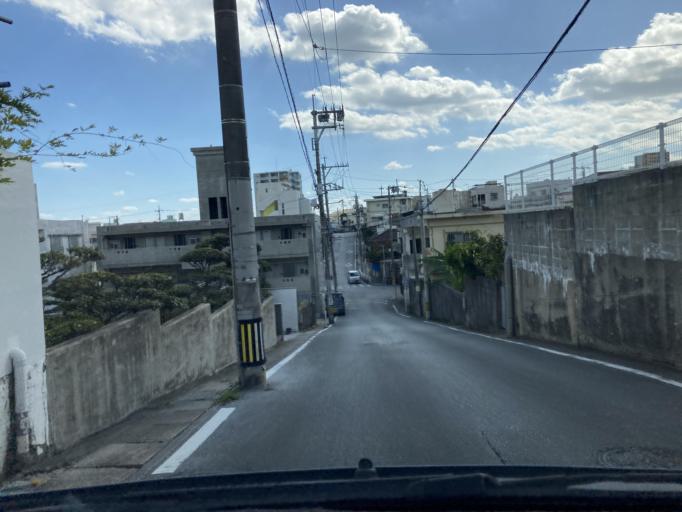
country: JP
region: Okinawa
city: Okinawa
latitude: 26.3404
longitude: 127.8069
